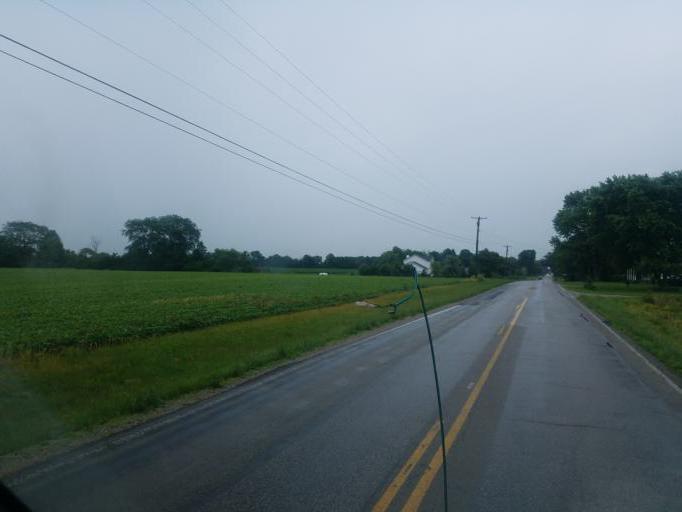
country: US
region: Ohio
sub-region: Marion County
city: Marion
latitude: 40.5495
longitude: -83.0949
